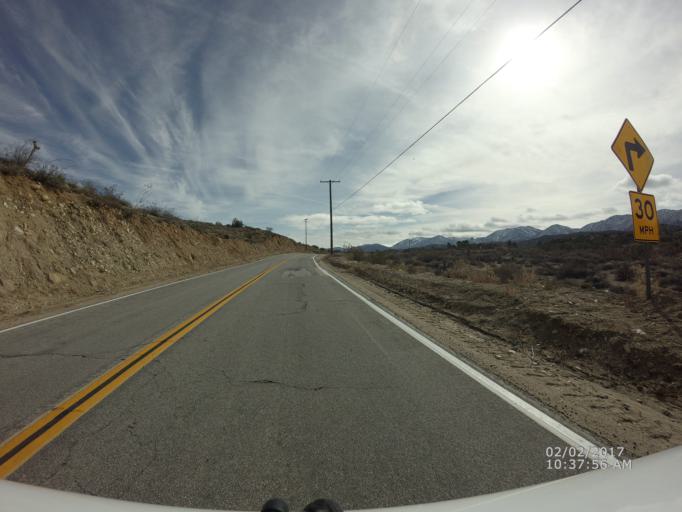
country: US
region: California
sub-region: Los Angeles County
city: Littlerock
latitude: 34.4805
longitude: -117.9377
